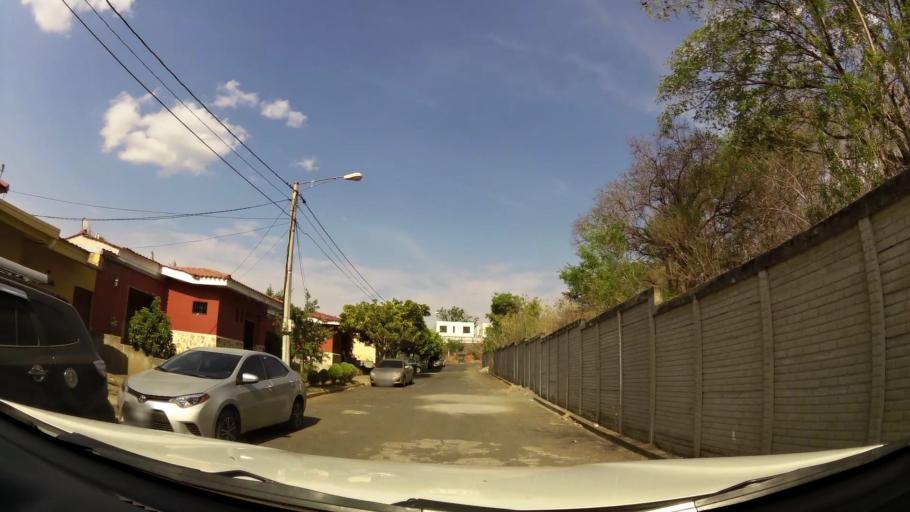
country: NI
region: Managua
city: Managua
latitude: 12.1020
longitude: -86.2720
